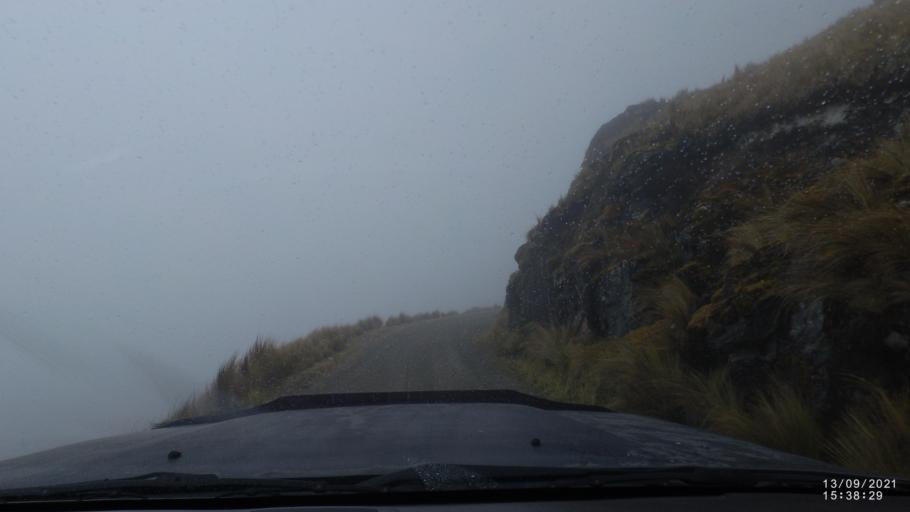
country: BO
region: Cochabamba
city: Colomi
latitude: -17.3278
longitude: -65.7227
